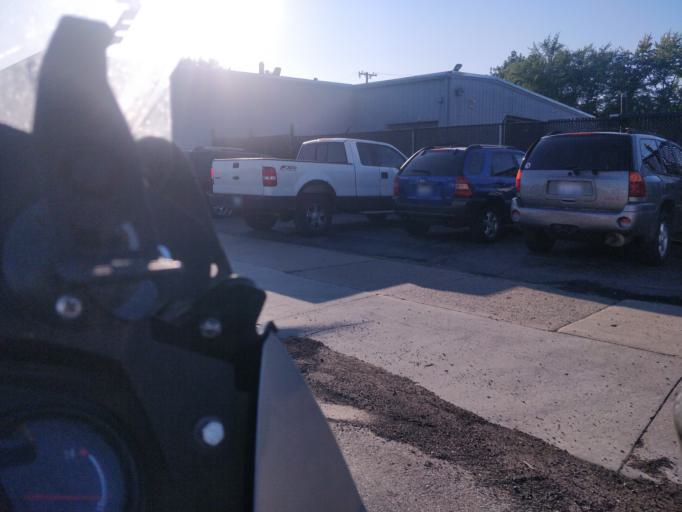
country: US
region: Michigan
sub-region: Wayne County
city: Melvindale
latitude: 42.2861
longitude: -83.1841
